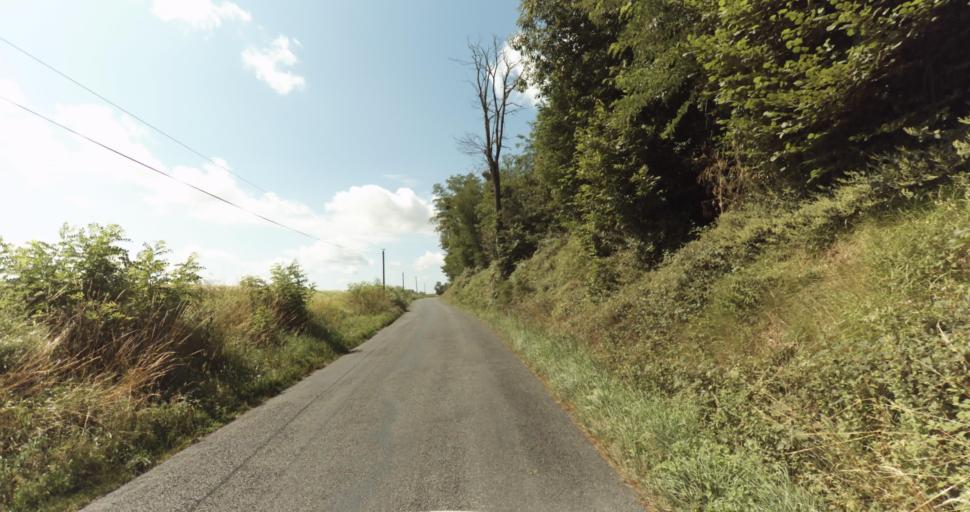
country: FR
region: Aquitaine
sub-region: Departement de la Gironde
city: Bazas
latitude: 44.4527
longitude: -0.2067
